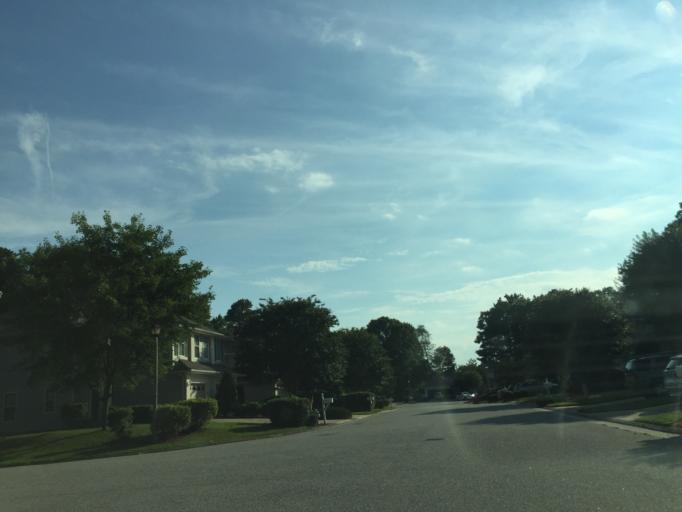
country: US
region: Virginia
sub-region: York County
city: Yorktown
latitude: 37.1169
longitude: -76.4804
